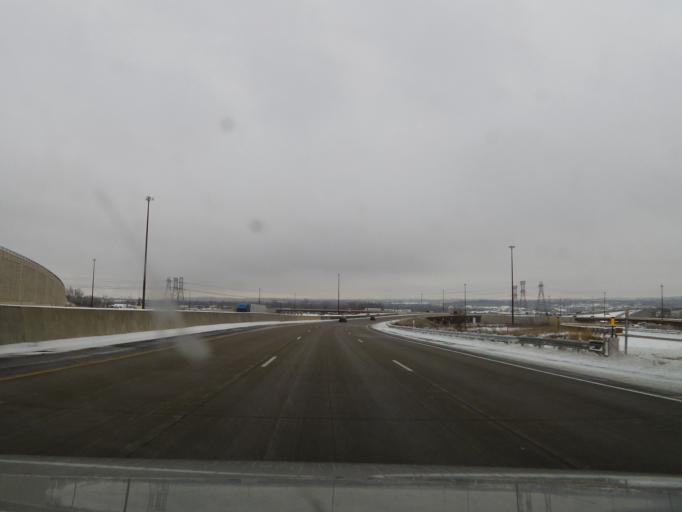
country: US
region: Minnesota
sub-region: Washington County
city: Newport
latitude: 44.8884
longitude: -93.0013
